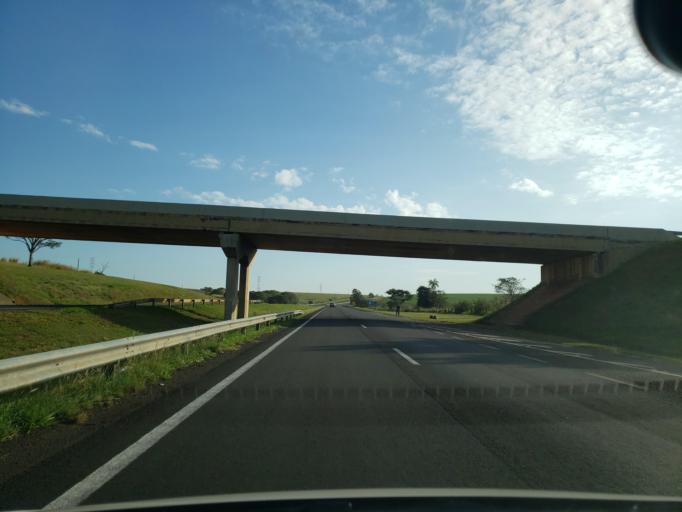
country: BR
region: Sao Paulo
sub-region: Valparaiso
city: Valparaiso
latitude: -21.2151
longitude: -50.8388
